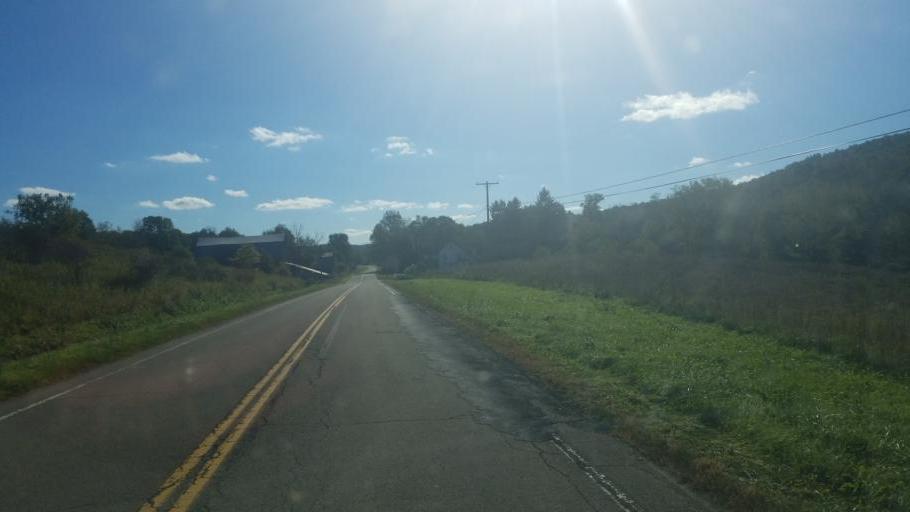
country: US
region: New York
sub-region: Allegany County
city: Friendship
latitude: 42.2848
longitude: -78.1234
